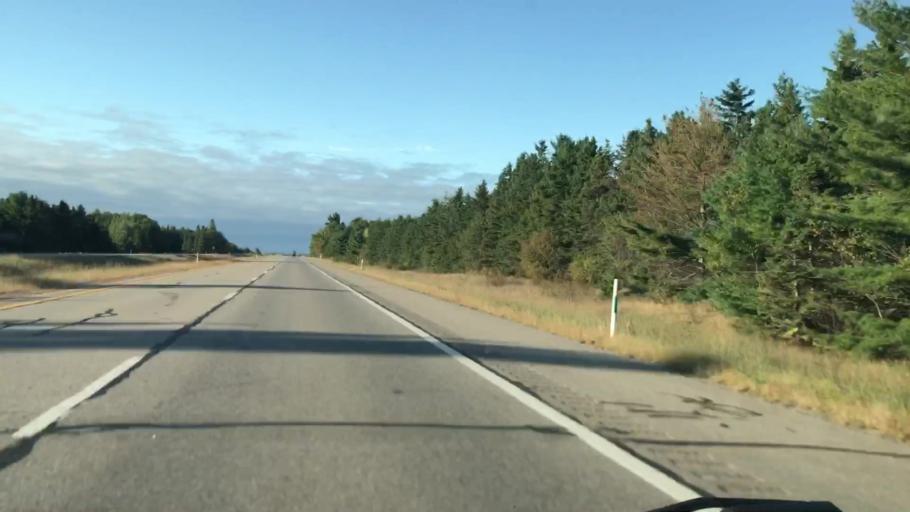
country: US
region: Michigan
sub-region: Chippewa County
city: Sault Ste. Marie
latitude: 46.4303
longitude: -84.3911
